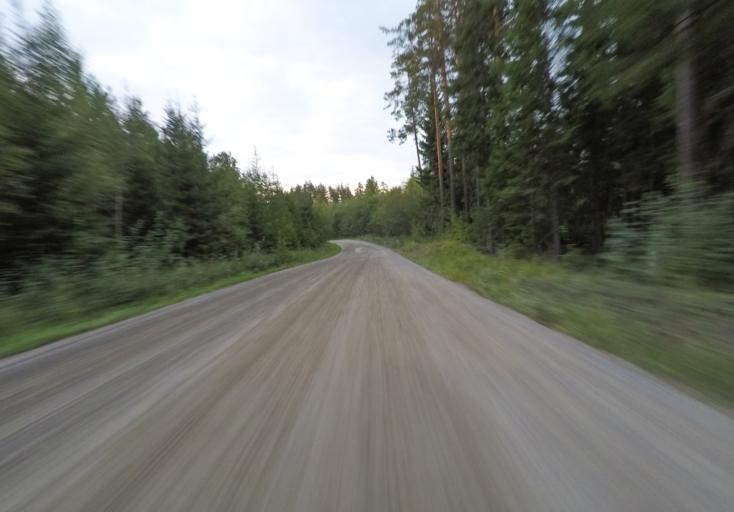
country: FI
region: Central Finland
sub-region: Jyvaeskylae
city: Hankasalmi
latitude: 62.4227
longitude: 26.6482
